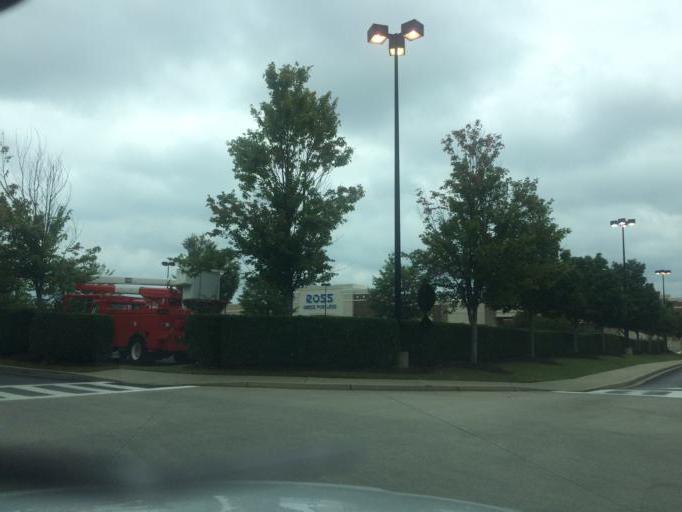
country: US
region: South Carolina
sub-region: Greenville County
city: Mauldin
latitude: 34.8289
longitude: -82.2968
